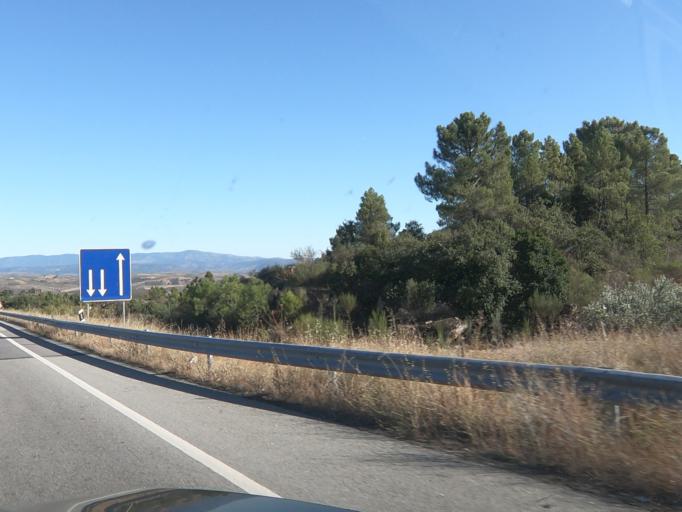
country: PT
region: Vila Real
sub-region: Valpacos
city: Valpacos
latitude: 41.5697
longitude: -7.2885
